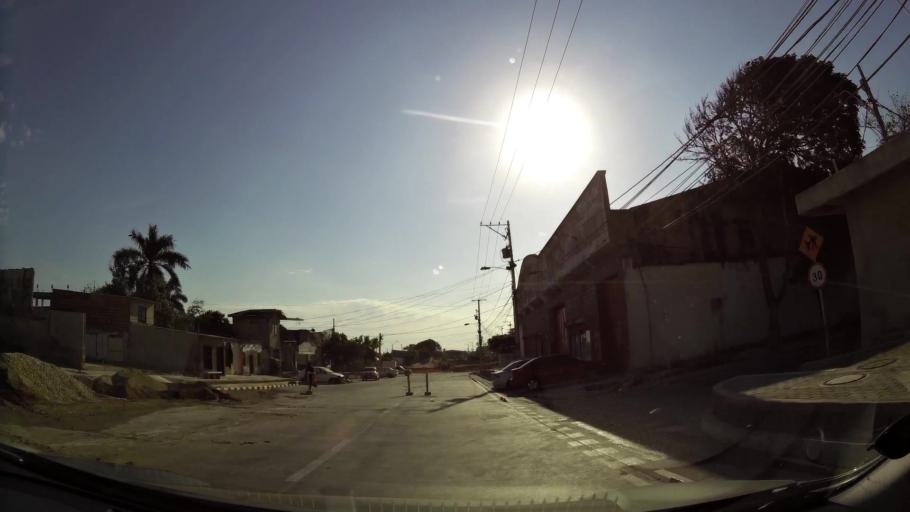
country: CO
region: Atlantico
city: Barranquilla
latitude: 10.9903
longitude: -74.7873
